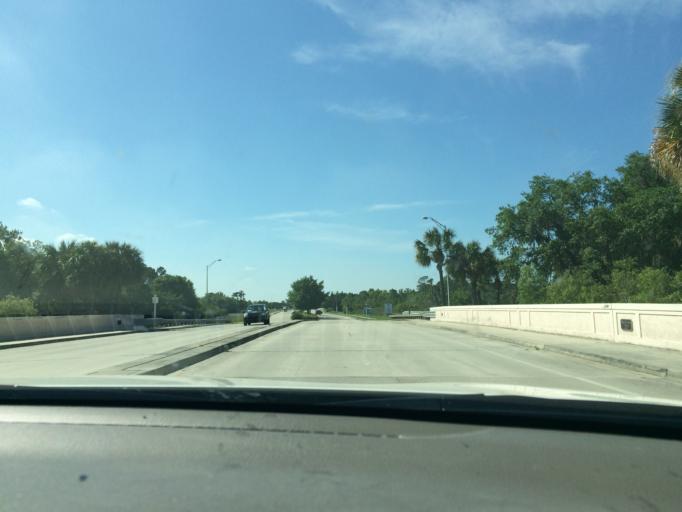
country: US
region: Florida
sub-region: Sarasota County
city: The Meadows
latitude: 27.4184
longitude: -82.3996
